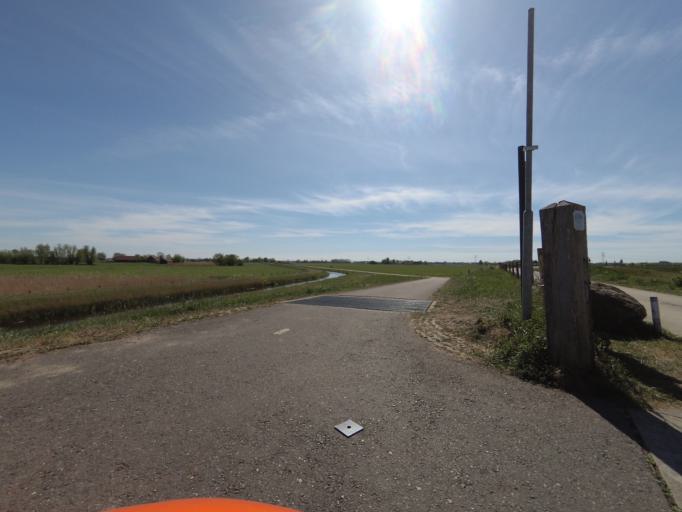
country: NL
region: Utrecht
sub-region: Gemeente Bunschoten
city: Bunschoten
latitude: 52.2468
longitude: 5.4042
